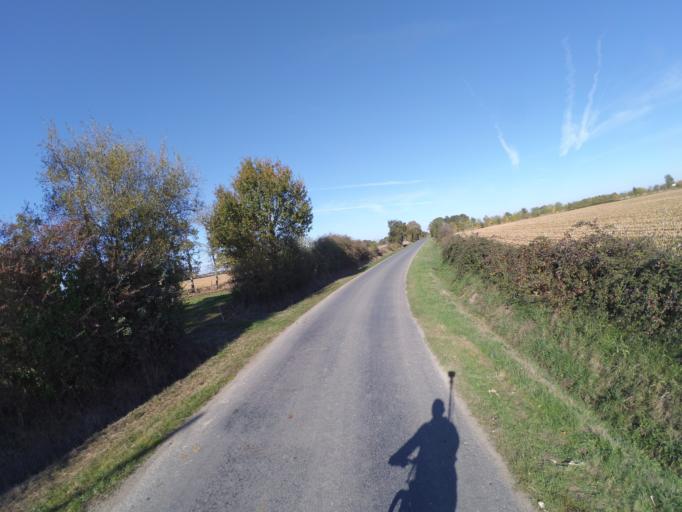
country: FR
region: Pays de la Loire
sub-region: Departement de la Loire-Atlantique
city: Saint-Lumine-de-Clisson
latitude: 47.0655
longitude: -1.3369
